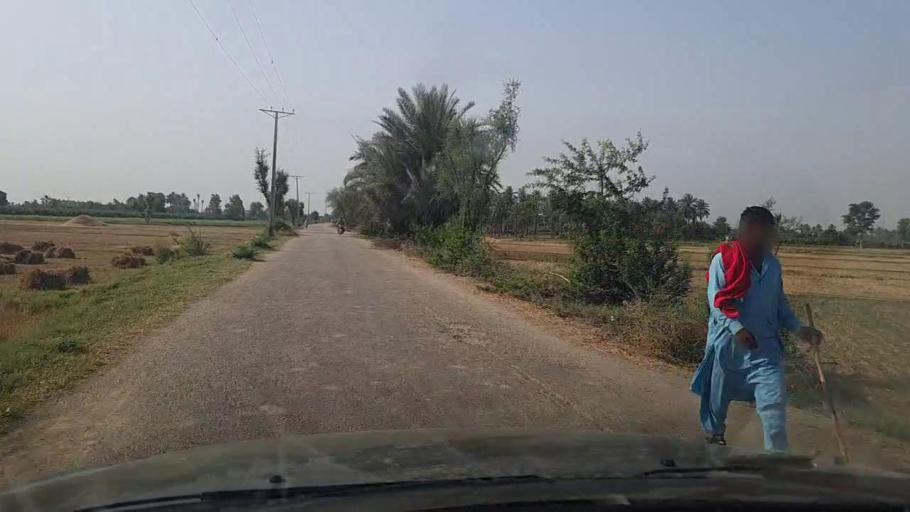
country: PK
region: Sindh
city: Kot Diji
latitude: 27.2778
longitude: 68.6510
